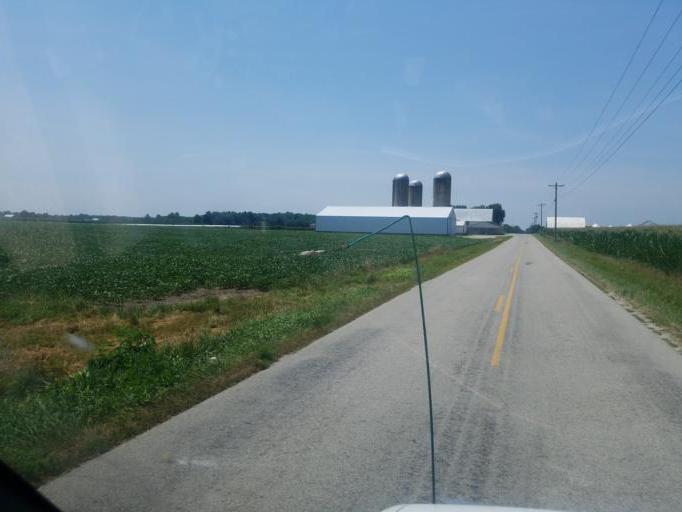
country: US
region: Ohio
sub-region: Shelby County
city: Fort Loramie
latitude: 40.3291
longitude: -84.3536
